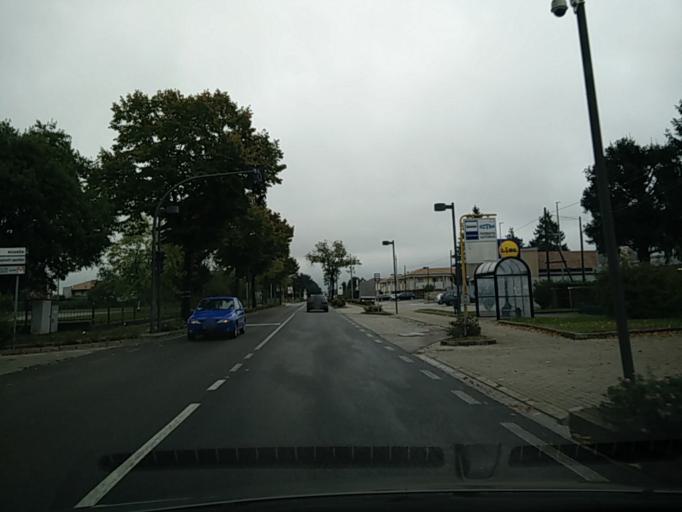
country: IT
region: Veneto
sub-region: Provincia di Treviso
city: Vedelago
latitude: 45.6867
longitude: 12.0237
